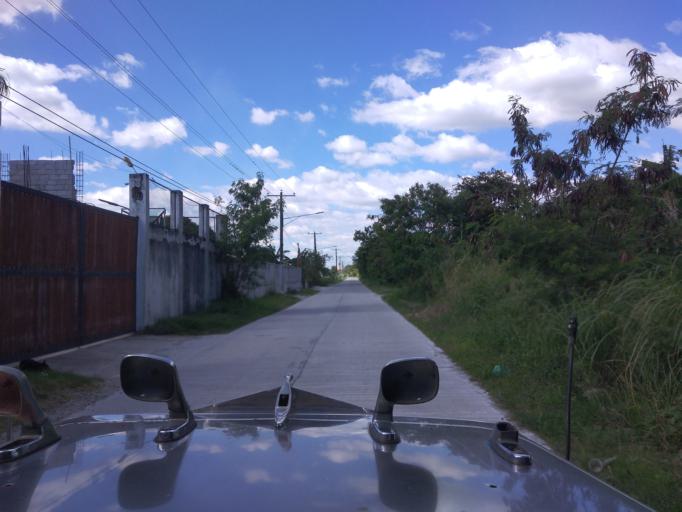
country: PH
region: Central Luzon
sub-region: Province of Pampanga
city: Bacolor
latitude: 15.0182
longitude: 120.6405
